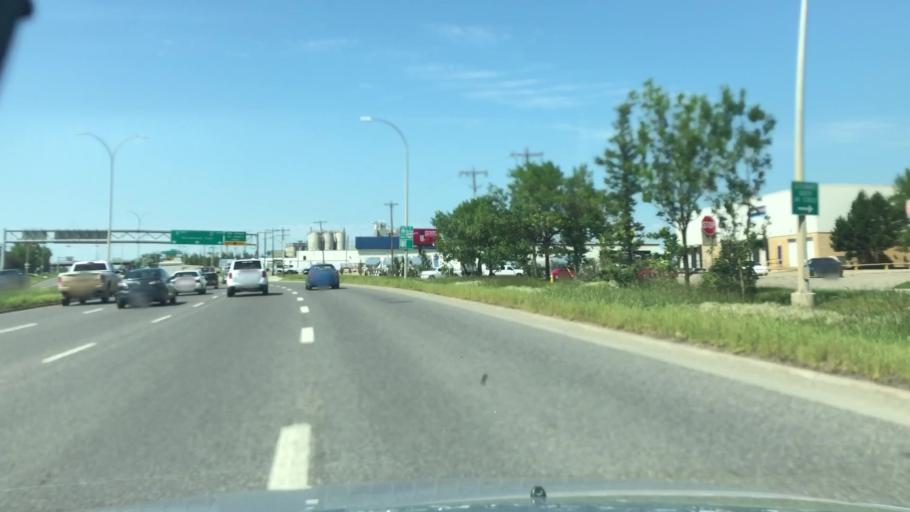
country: CA
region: Alberta
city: St. Albert
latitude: 53.5814
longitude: -113.5809
